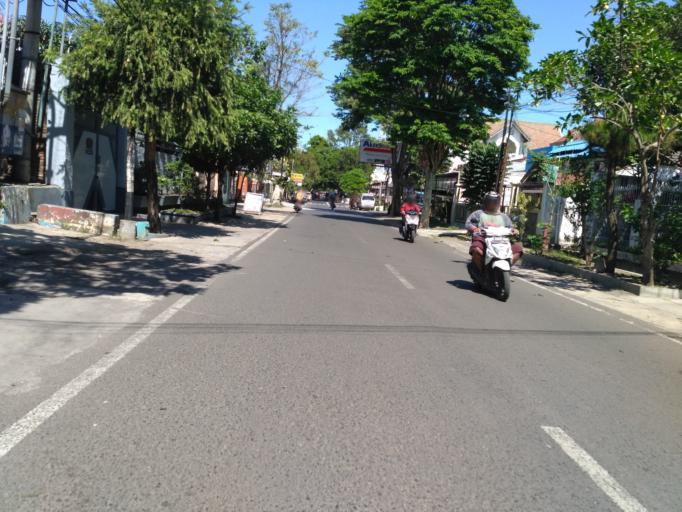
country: ID
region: East Java
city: Malang
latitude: -7.9773
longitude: 112.6644
